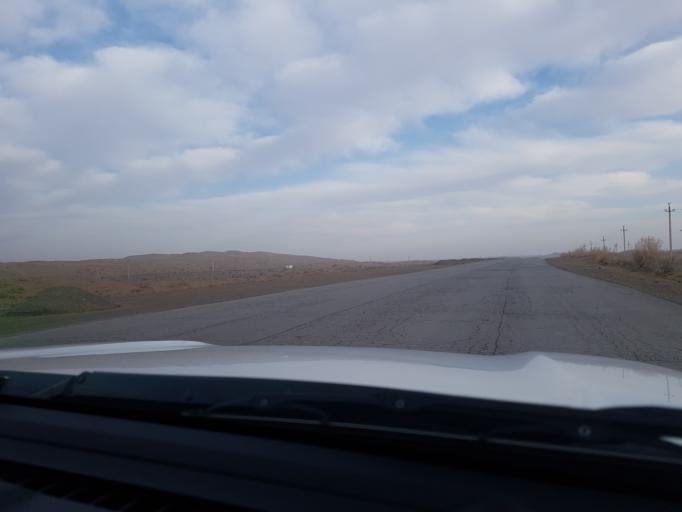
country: TM
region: Ahal
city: Abadan
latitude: 38.7289
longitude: 58.4946
